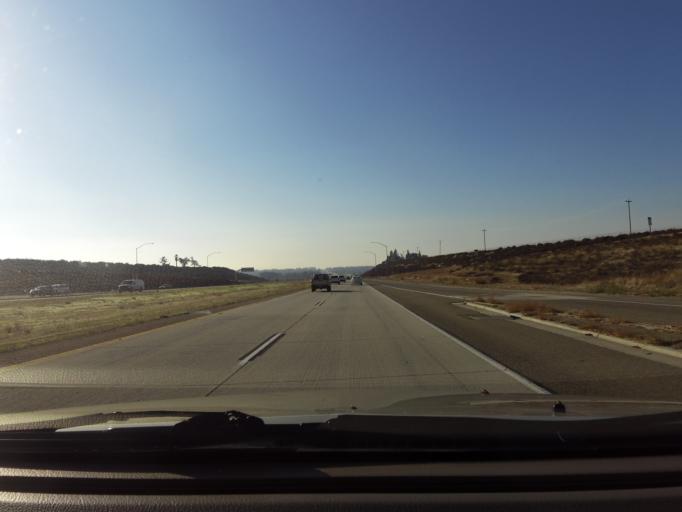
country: US
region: California
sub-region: Fresno County
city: Clovis
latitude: 36.8931
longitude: -119.7929
